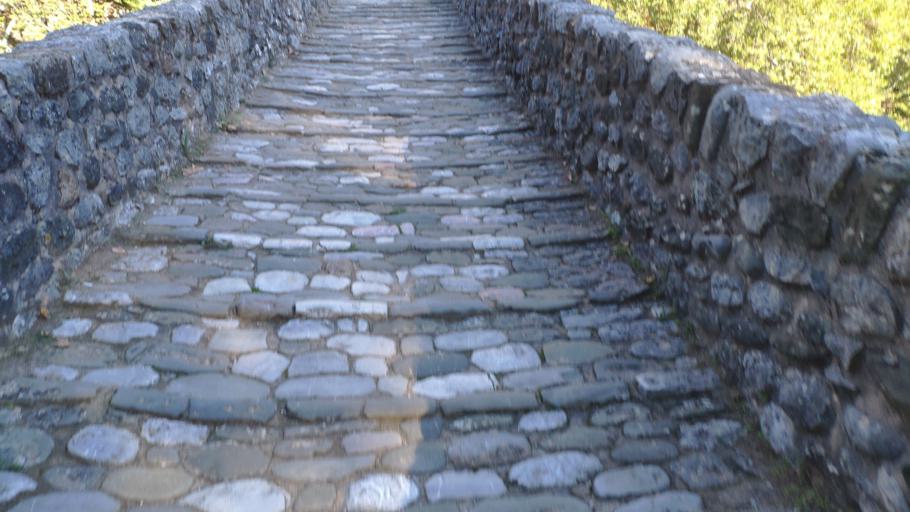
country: GR
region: Thessaly
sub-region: Trikala
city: Pyli
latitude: 39.4603
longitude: 21.6006
